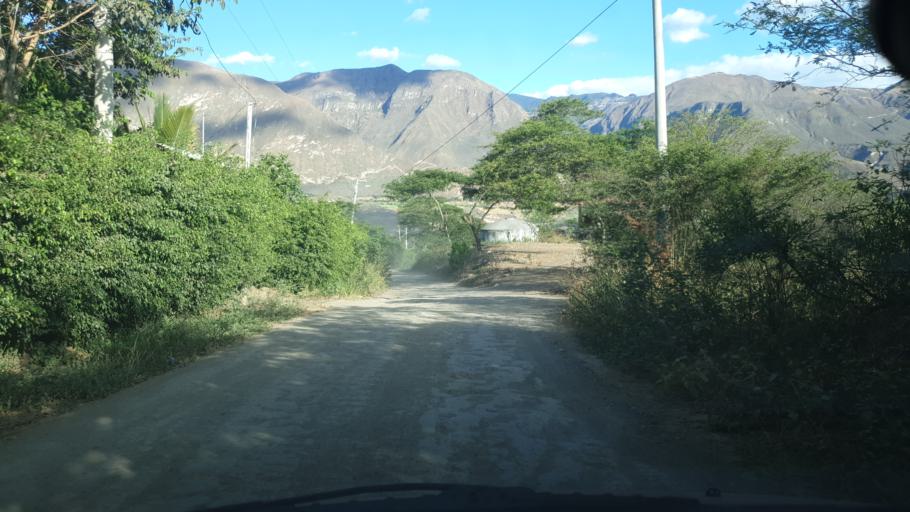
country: EC
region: Azuay
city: Cuenca
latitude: -3.2885
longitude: -79.2906
